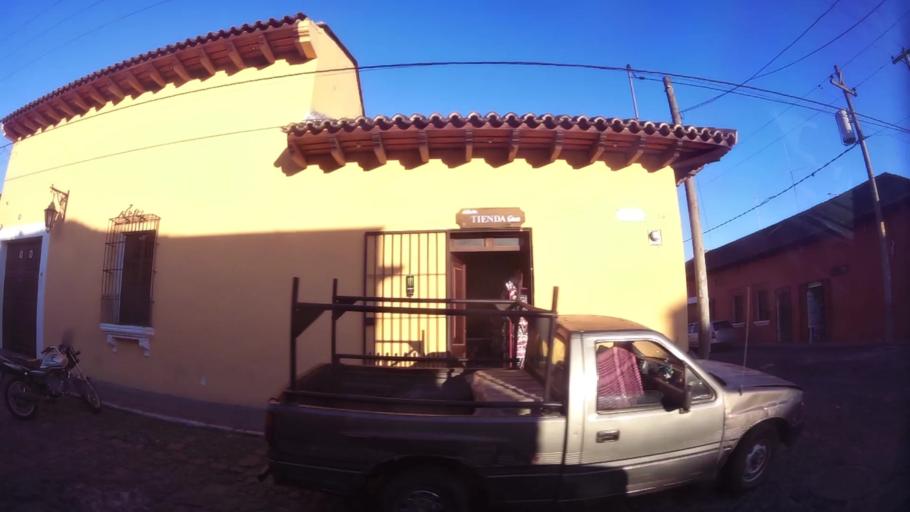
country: GT
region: Sacatepequez
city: Antigua Guatemala
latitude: 14.5594
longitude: -90.7353
